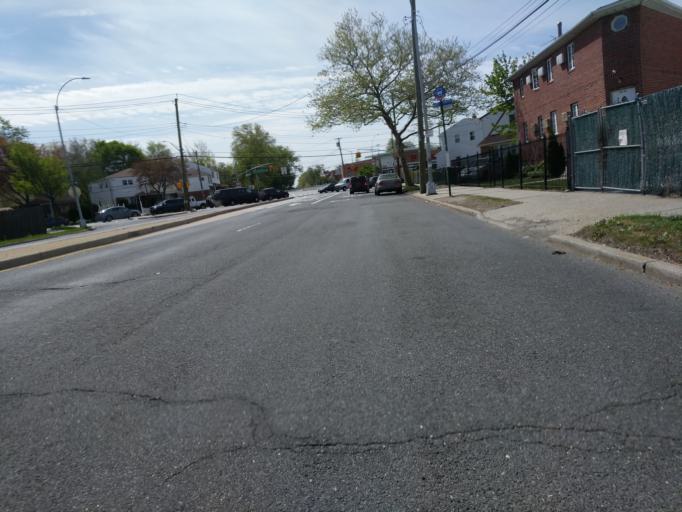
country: US
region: New York
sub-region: Nassau County
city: Bellerose Terrace
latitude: 40.6939
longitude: -73.7453
